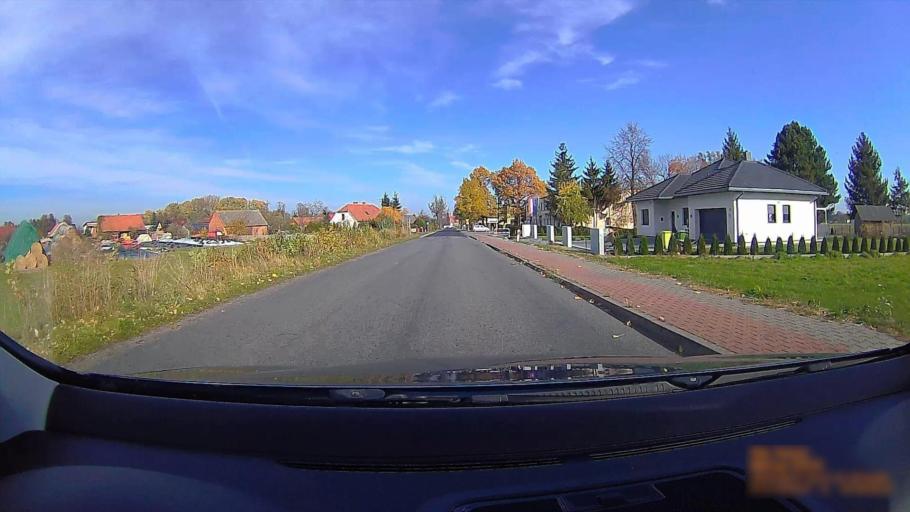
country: PL
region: Greater Poland Voivodeship
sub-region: Powiat ostrzeszowski
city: Doruchow
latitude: 51.4097
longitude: 18.0740
